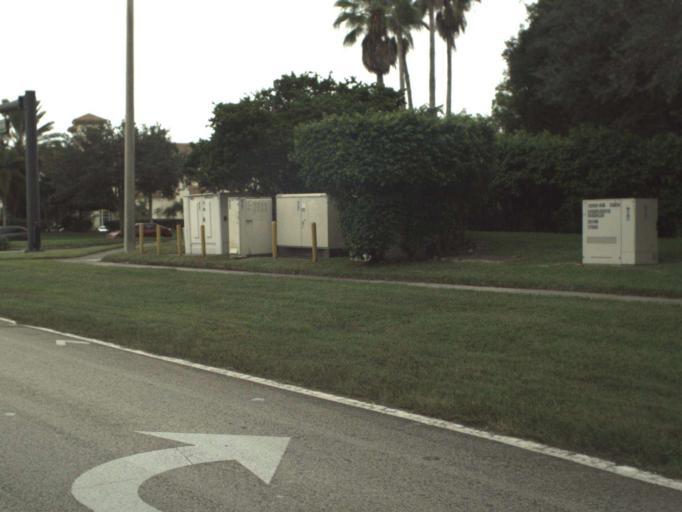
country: US
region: Florida
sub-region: Broward County
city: Coral Springs
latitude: 26.2331
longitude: -80.2923
